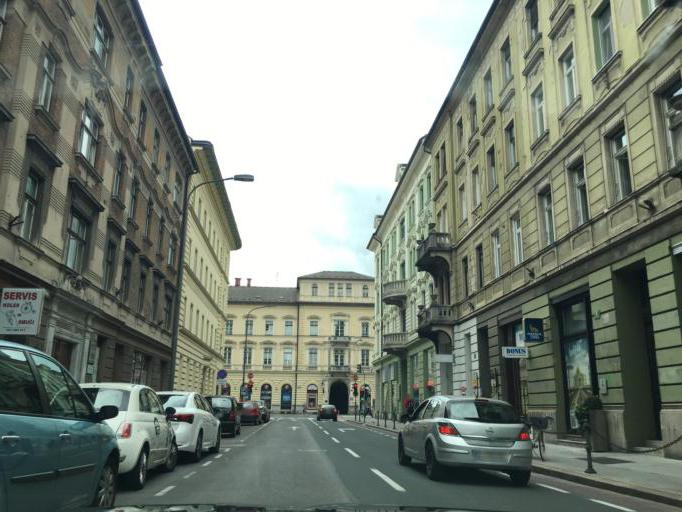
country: SI
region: Ljubljana
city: Ljubljana
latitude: 46.0548
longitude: 14.5057
